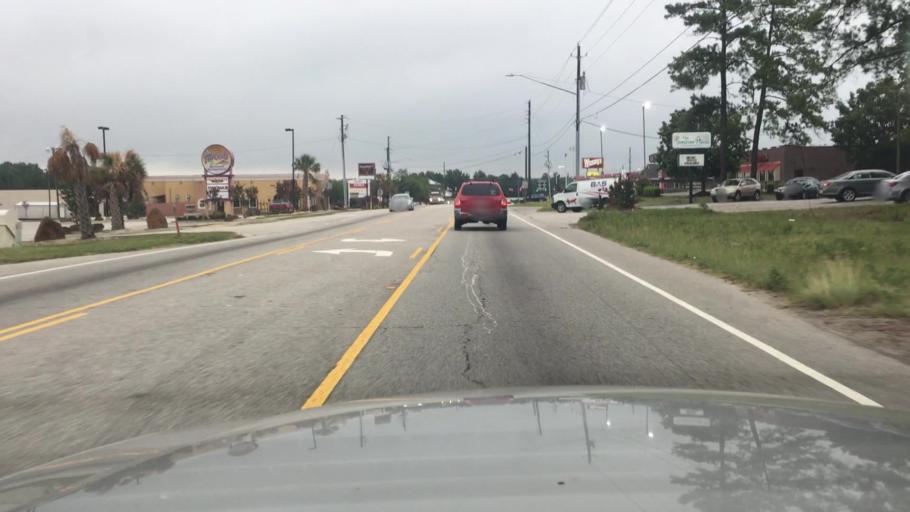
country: US
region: North Carolina
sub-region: Cumberland County
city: Hope Mills
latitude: 34.9845
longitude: -78.9679
